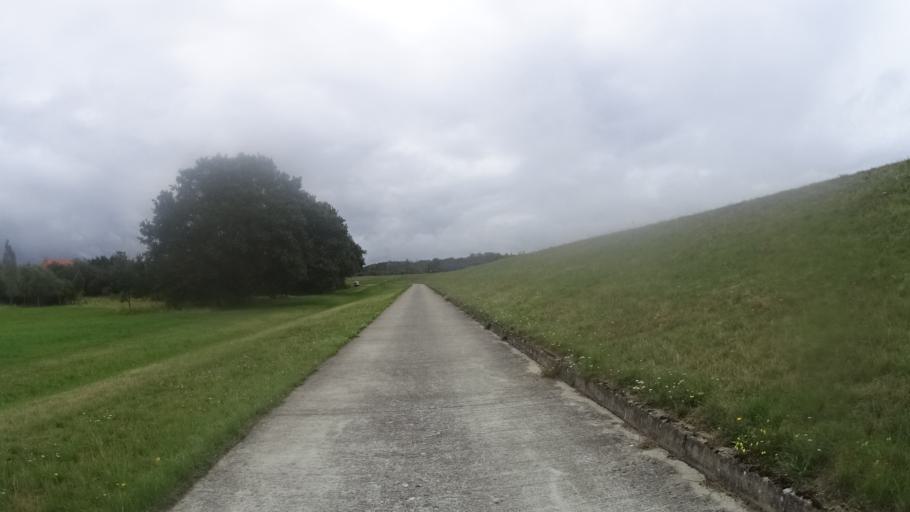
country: DE
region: Lower Saxony
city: Tosterglope
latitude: 53.2611
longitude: 10.8311
